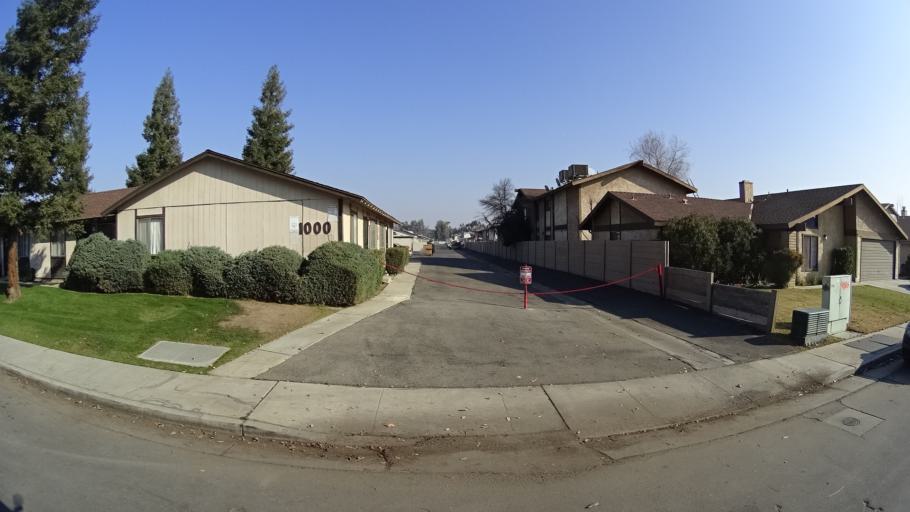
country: US
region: California
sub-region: Kern County
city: Bakersfield
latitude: 35.3450
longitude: -119.0529
